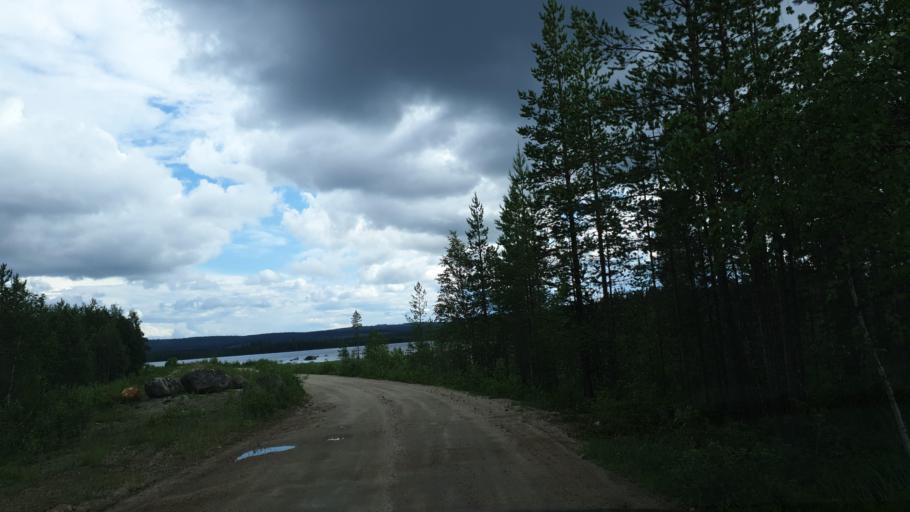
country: SE
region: Jaemtland
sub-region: Harjedalens Kommun
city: Sveg
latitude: 62.0438
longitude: 14.4820
